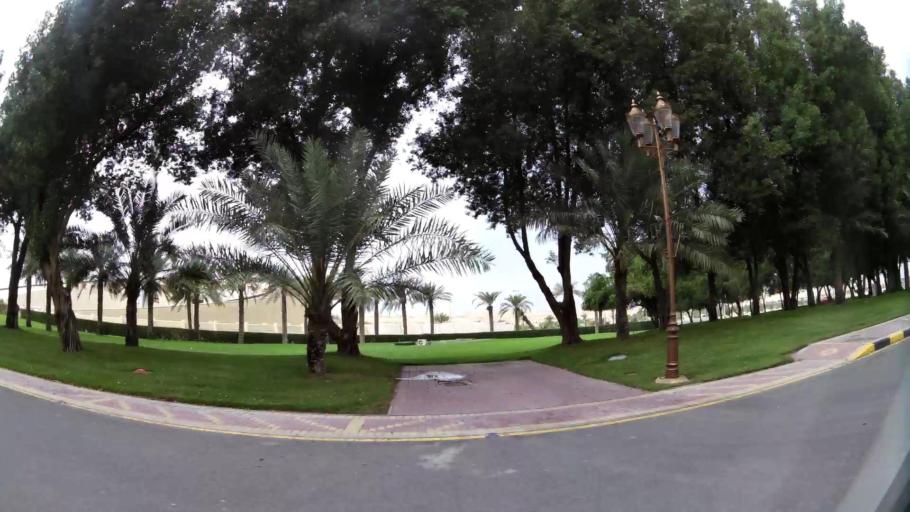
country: BH
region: Central Governorate
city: Dar Kulayb
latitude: 26.0721
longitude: 50.5278
